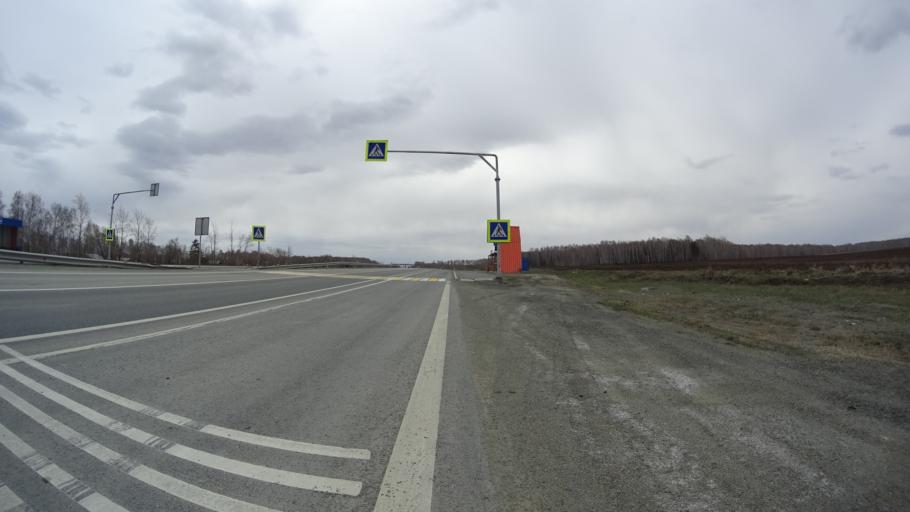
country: RU
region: Chelyabinsk
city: Yemanzhelinka
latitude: 54.8240
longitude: 61.3095
